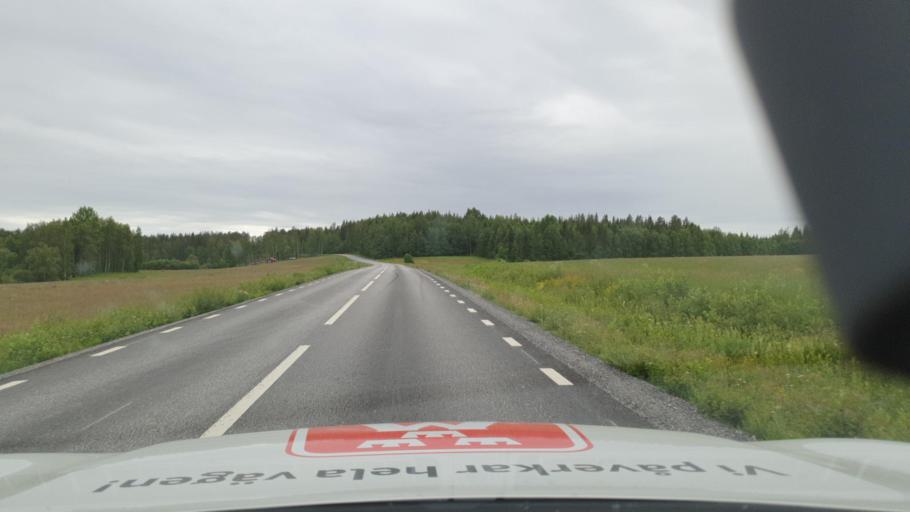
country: SE
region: Vaesterbotten
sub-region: Nordmalings Kommun
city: Nordmaling
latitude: 63.7175
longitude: 19.6369
